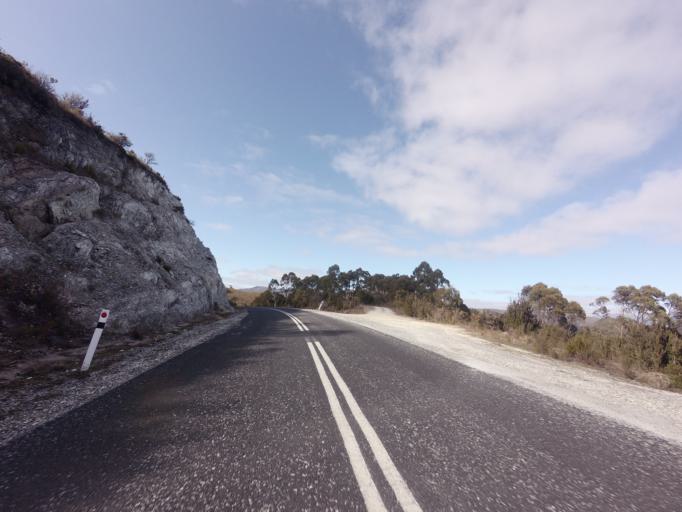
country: AU
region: Tasmania
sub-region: Huon Valley
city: Geeveston
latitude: -42.8329
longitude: 146.1253
